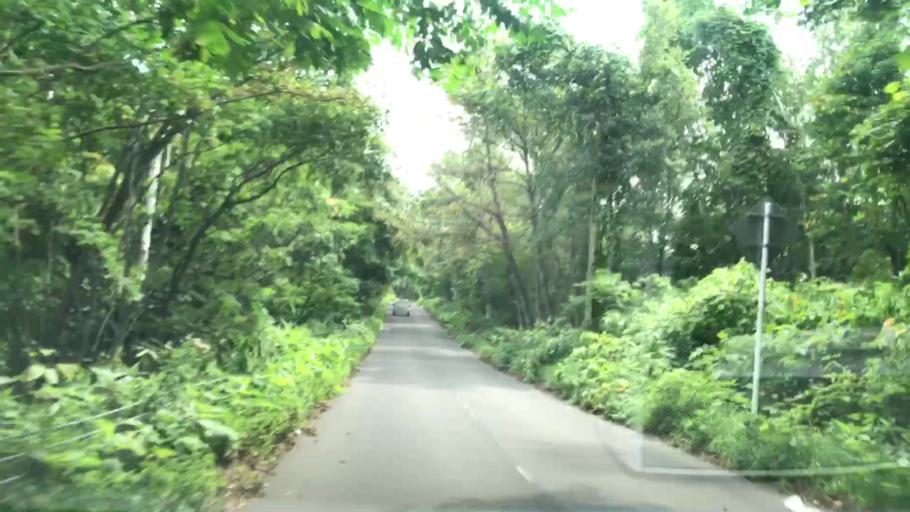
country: JP
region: Hokkaido
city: Yoichi
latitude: 43.1363
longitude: 140.8217
